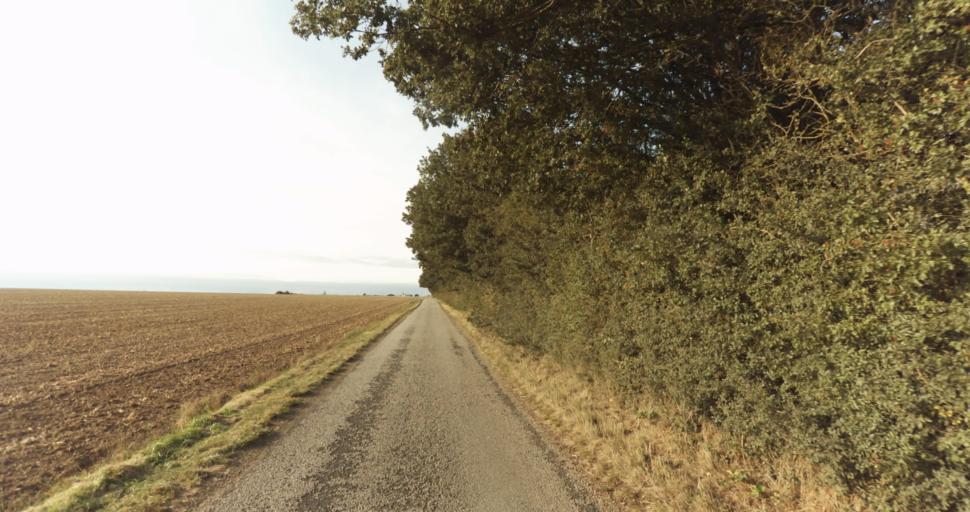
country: FR
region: Haute-Normandie
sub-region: Departement de l'Eure
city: Marcilly-sur-Eure
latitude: 48.8818
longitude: 1.2783
